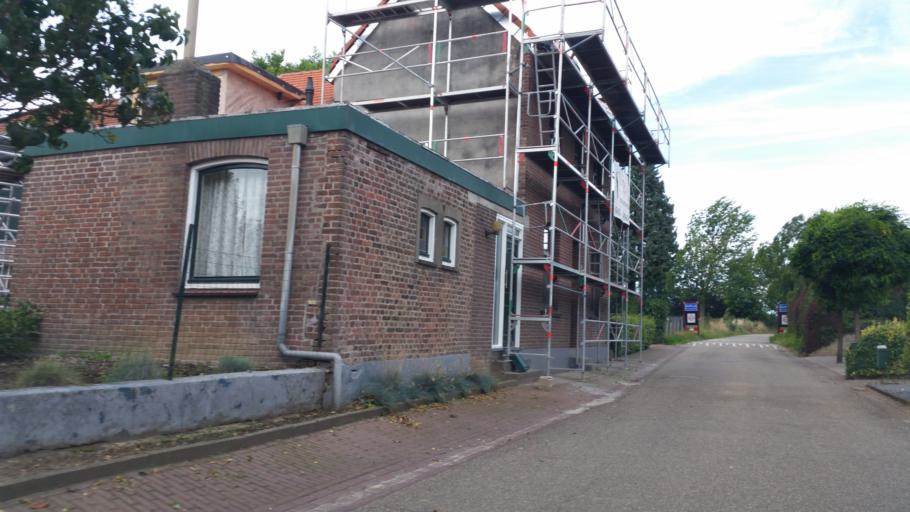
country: NL
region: Limburg
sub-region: Eijsden-Margraten
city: Margraten
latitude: 50.8316
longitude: 5.8097
